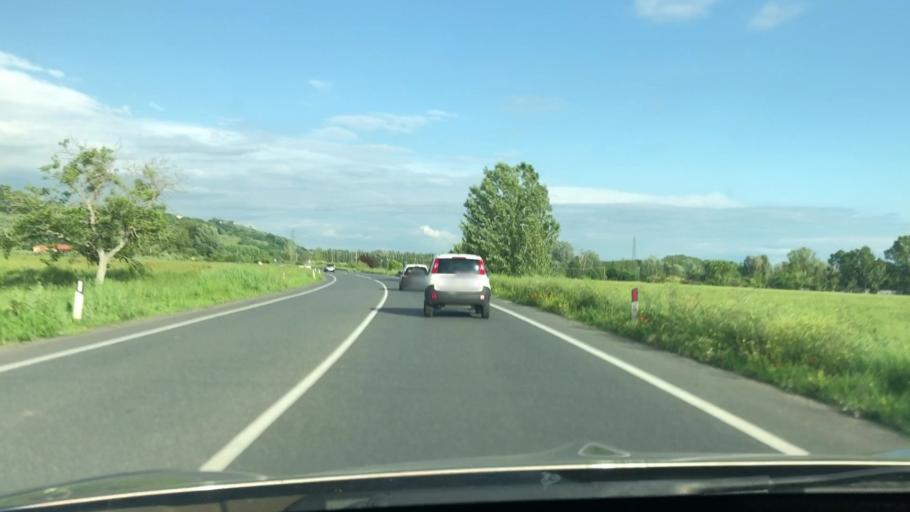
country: IT
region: Tuscany
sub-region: Province of Pisa
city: Treggiaia
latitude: 43.6196
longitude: 10.6674
